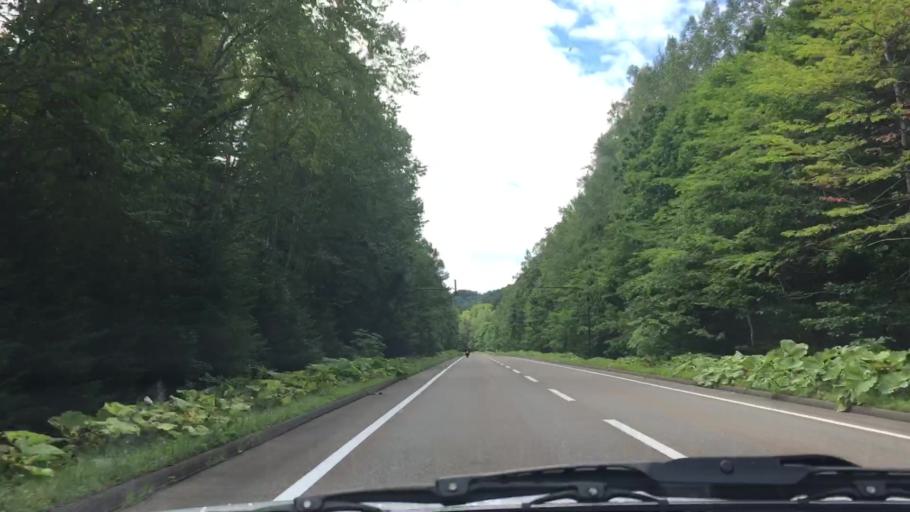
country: JP
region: Hokkaido
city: Kitami
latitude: 43.4011
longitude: 143.9295
